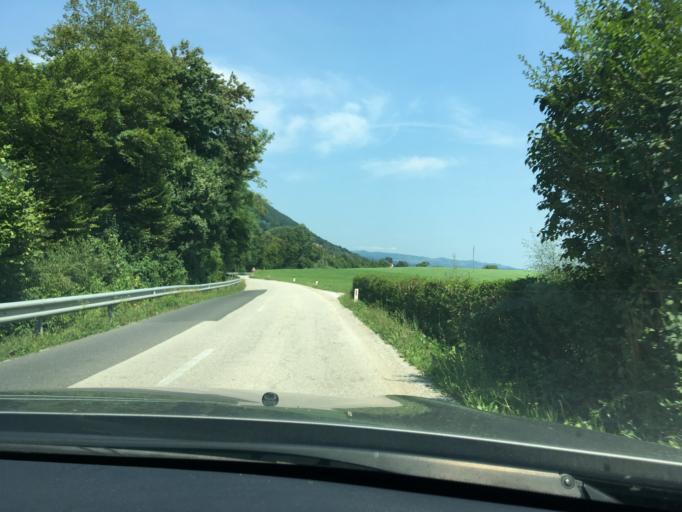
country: SI
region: Straza
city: Straza
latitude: 45.7757
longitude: 15.0606
